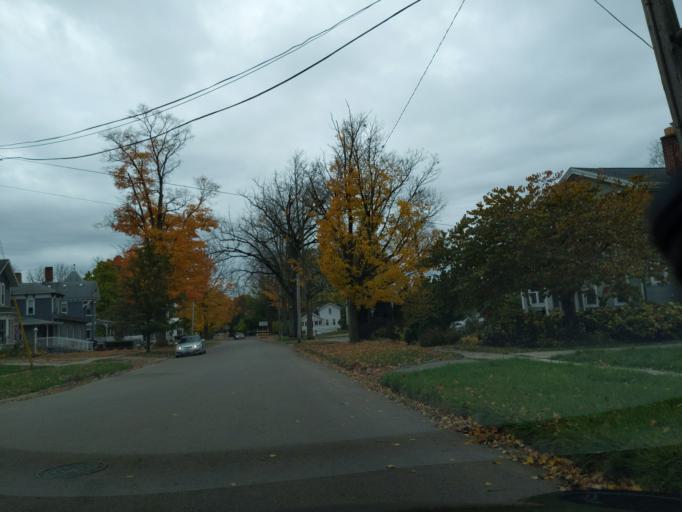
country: US
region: Michigan
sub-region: Eaton County
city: Eaton Rapids
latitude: 42.5104
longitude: -84.6532
